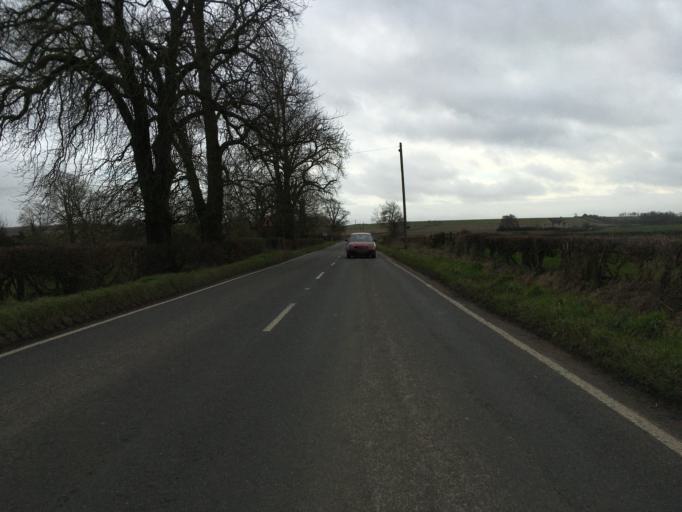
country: GB
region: England
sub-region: Gloucestershire
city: Lechlade
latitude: 51.6818
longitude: -1.6764
